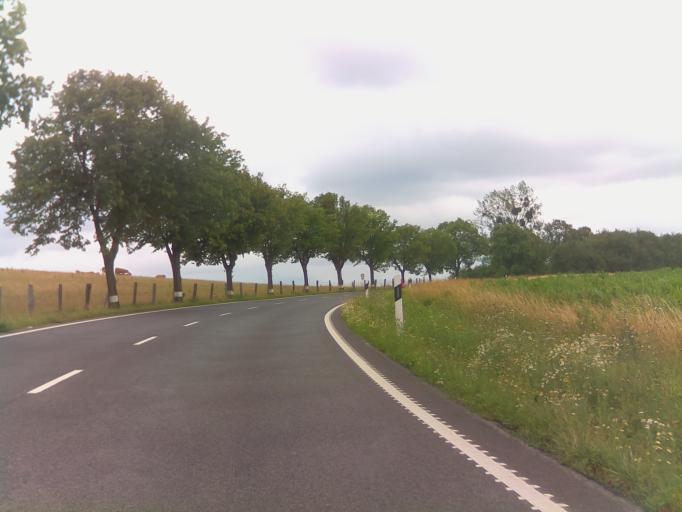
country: LU
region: Grevenmacher
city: Schengen
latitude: 49.4773
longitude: 6.3362
